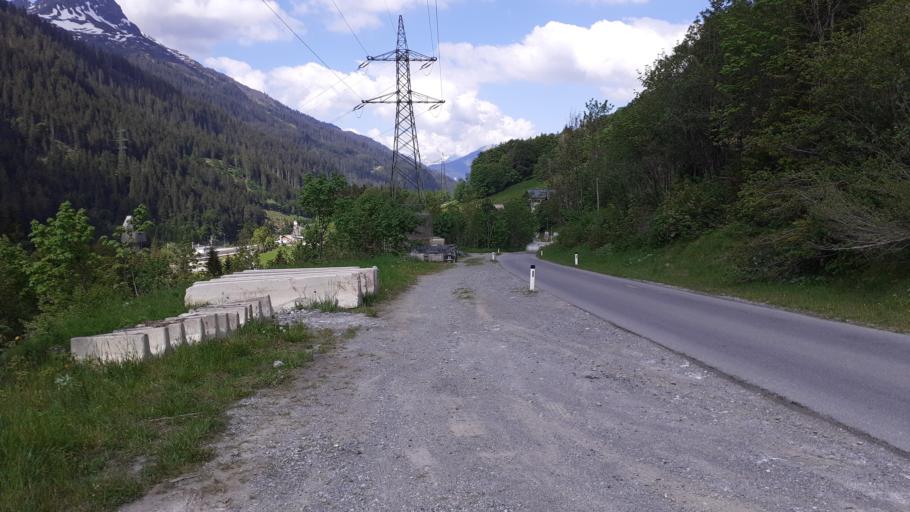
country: AT
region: Vorarlberg
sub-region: Politischer Bezirk Bludenz
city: Klosterle
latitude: 47.1338
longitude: 10.1289
